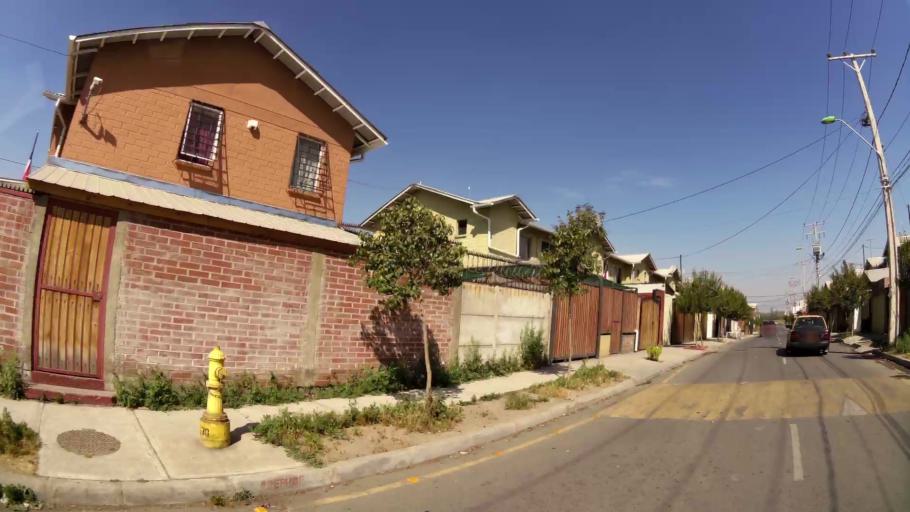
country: CL
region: Santiago Metropolitan
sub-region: Provincia de Santiago
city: La Pintana
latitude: -33.5643
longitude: -70.6271
